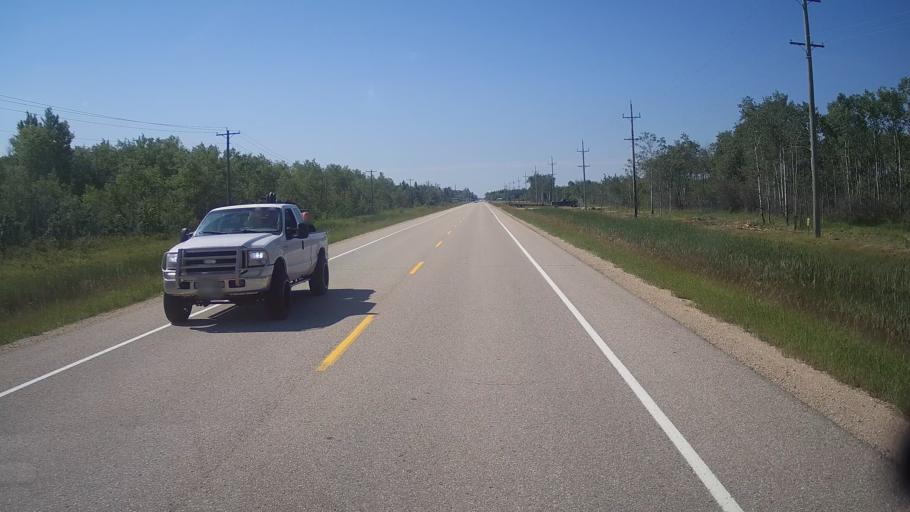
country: CA
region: Manitoba
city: La Broquerie
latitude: 49.6705
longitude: -96.4572
